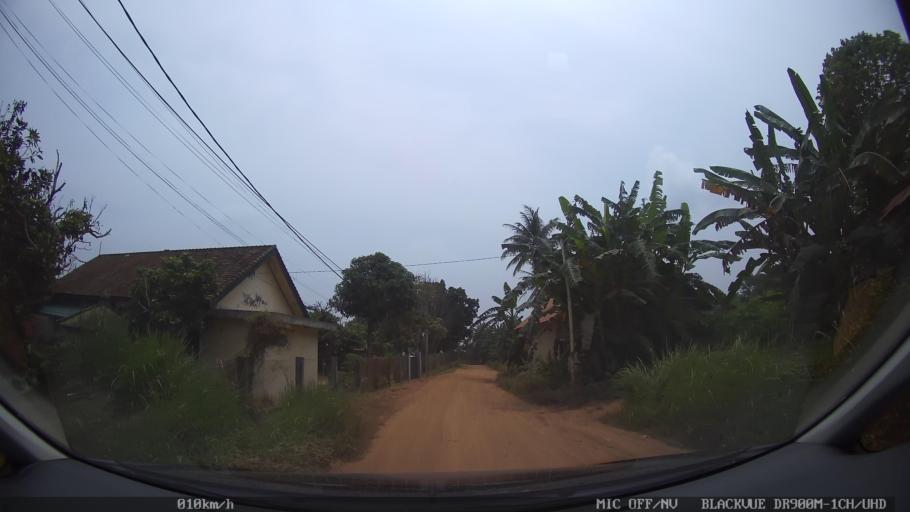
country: ID
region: Lampung
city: Kedaton
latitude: -5.3989
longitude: 105.3264
